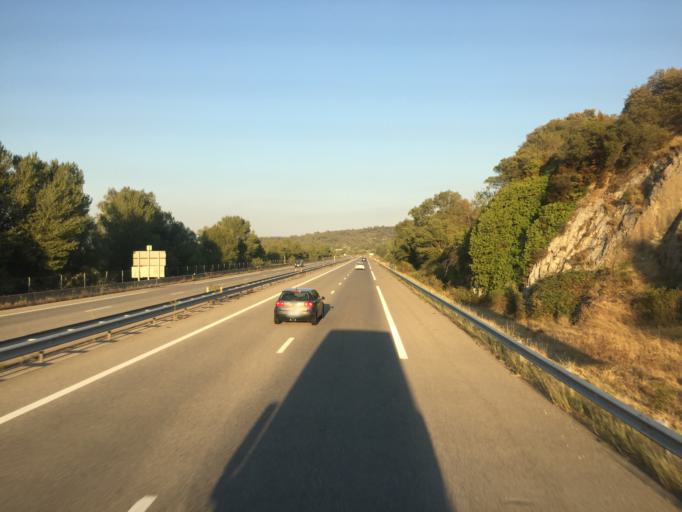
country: FR
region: Provence-Alpes-Cote d'Azur
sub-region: Departement du Vaucluse
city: Beaumont-de-Pertuis
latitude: 43.6897
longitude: 5.6977
